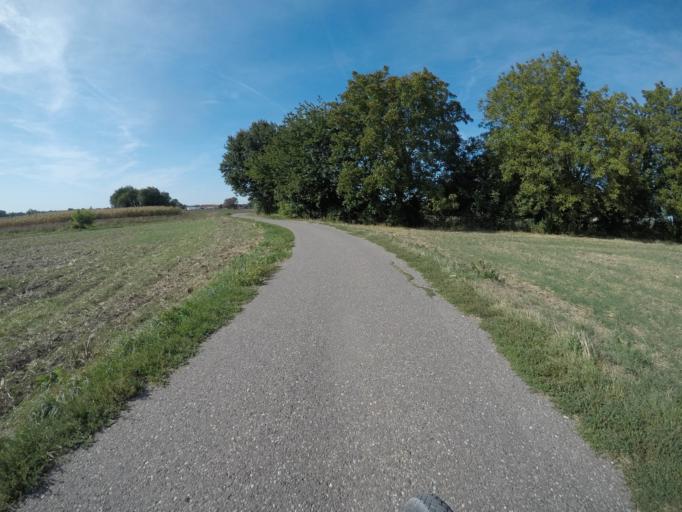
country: DE
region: Baden-Wuerttemberg
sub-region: Karlsruhe Region
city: Reilingen
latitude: 49.2891
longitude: 8.5795
